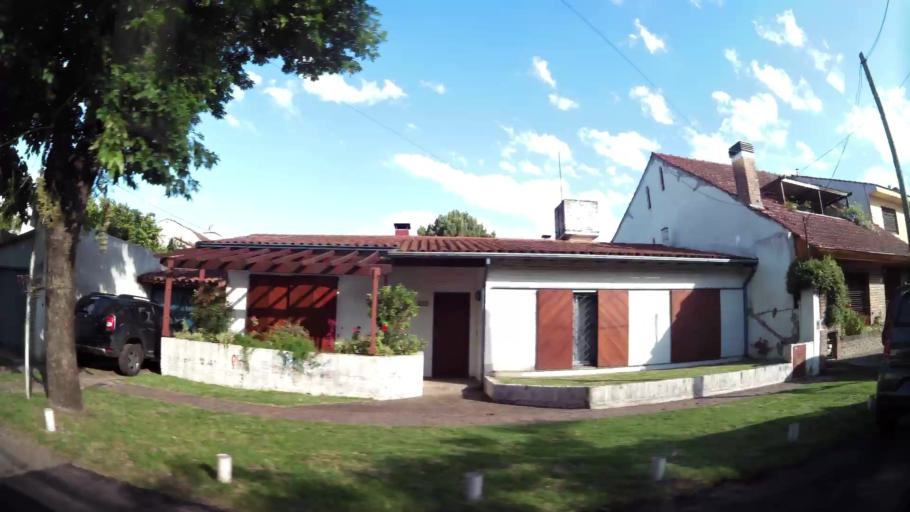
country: AR
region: Buenos Aires
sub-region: Partido de San Isidro
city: San Isidro
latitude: -34.4953
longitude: -58.5501
